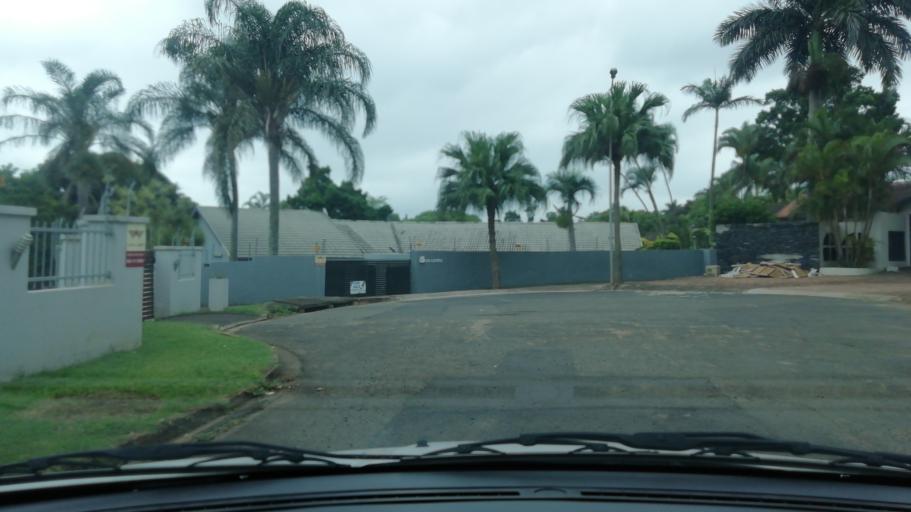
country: ZA
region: KwaZulu-Natal
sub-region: uThungulu District Municipality
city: Empangeni
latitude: -28.7652
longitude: 31.8907
